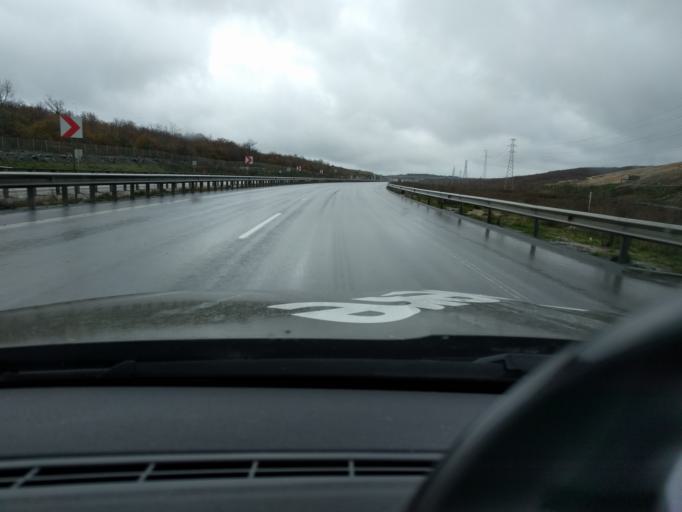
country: TR
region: Istanbul
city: Kemerburgaz
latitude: 41.2204
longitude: 28.8416
